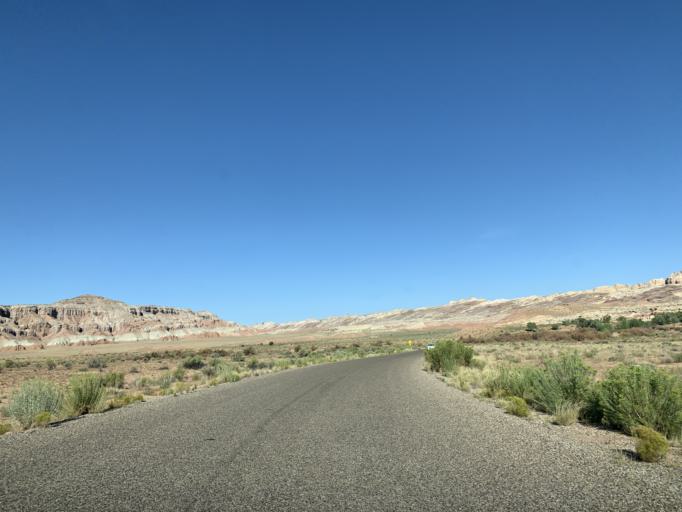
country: US
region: Utah
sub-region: Emery County
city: Ferron
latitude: 38.5755
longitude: -110.7426
